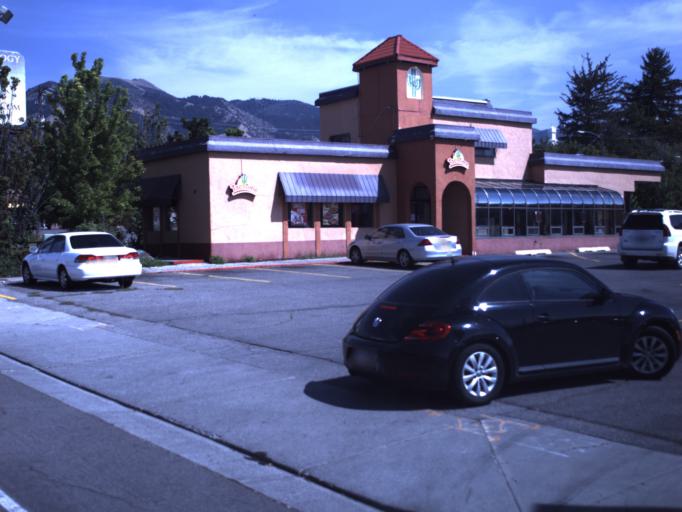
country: US
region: Utah
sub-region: Cache County
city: Logan
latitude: 41.7390
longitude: -111.8328
